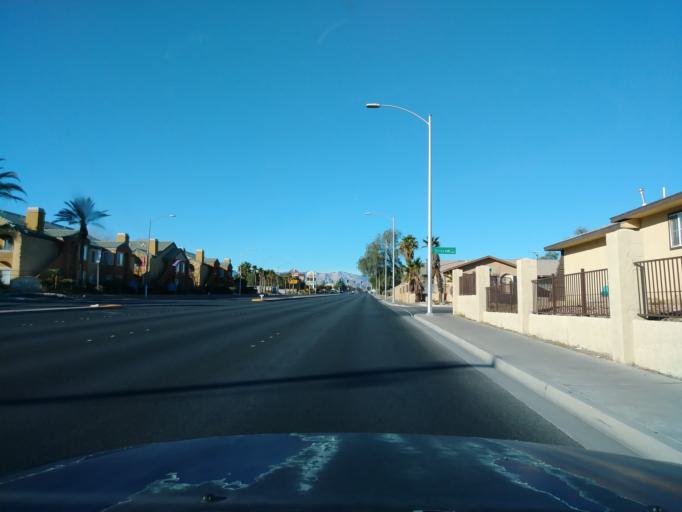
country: US
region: Nevada
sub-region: Clark County
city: Spring Valley
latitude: 36.1592
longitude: -115.2479
